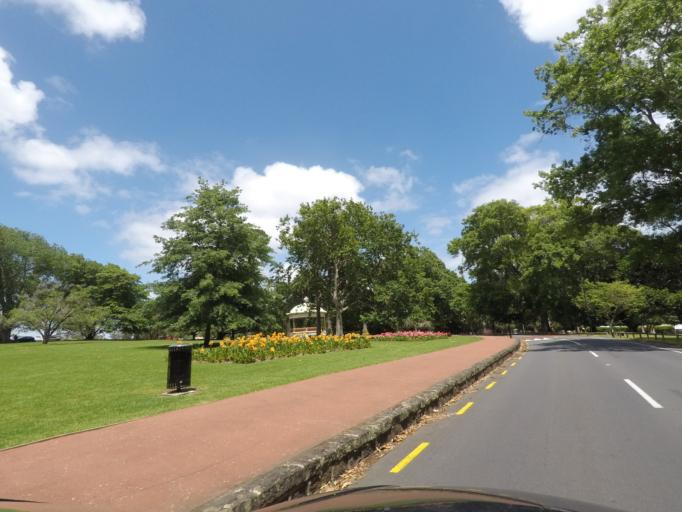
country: NZ
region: Auckland
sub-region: Auckland
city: Auckland
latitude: -36.8584
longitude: 174.7762
